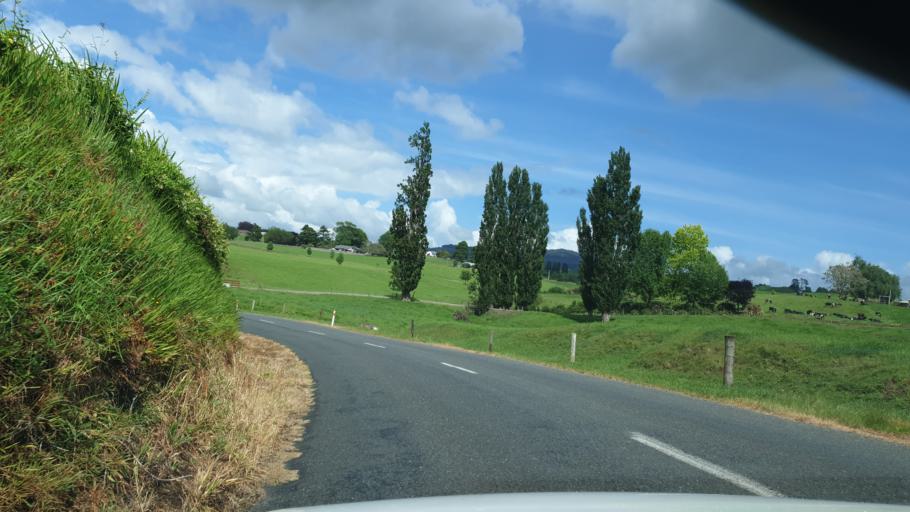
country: NZ
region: Waikato
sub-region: Matamata-Piako District
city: Matamata
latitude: -37.8264
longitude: 175.7328
